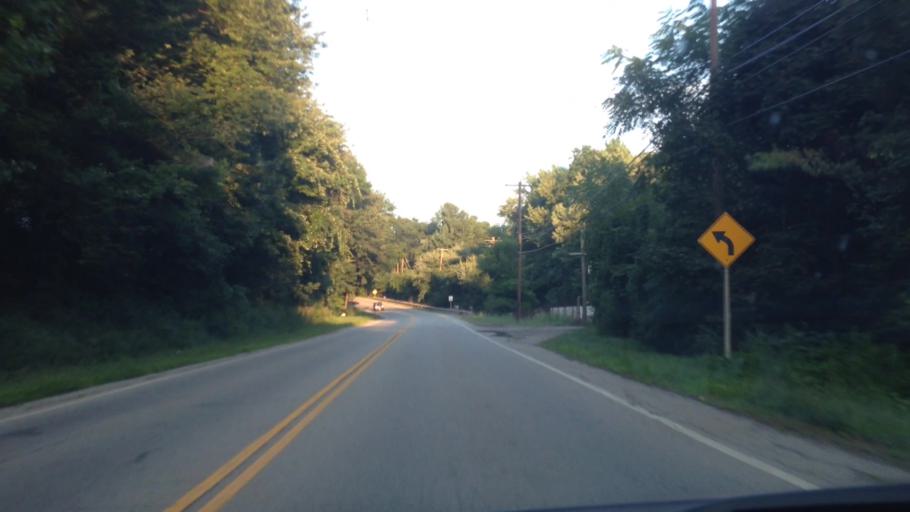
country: US
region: Ohio
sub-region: Summit County
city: Portage Lakes
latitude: 40.9817
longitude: -81.5544
